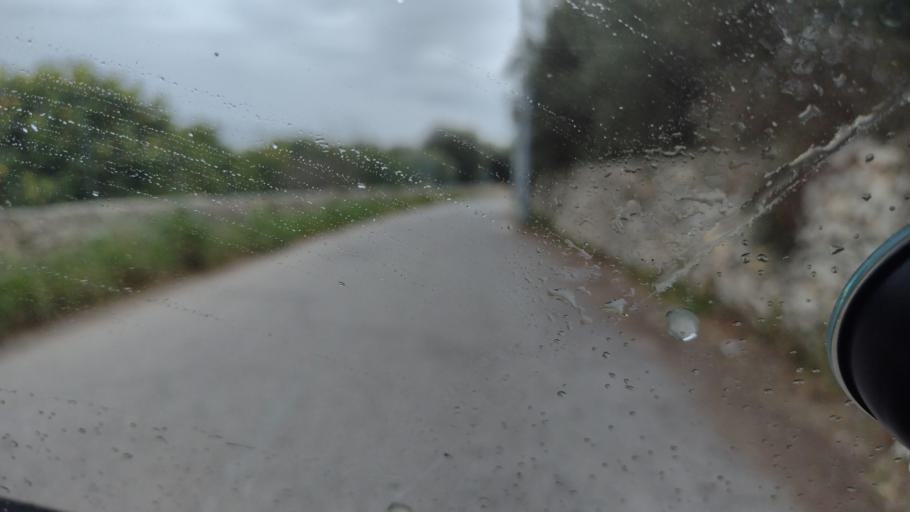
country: IT
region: Sicily
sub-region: Provincia di Siracusa
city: Avola
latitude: 36.8851
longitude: 15.1278
